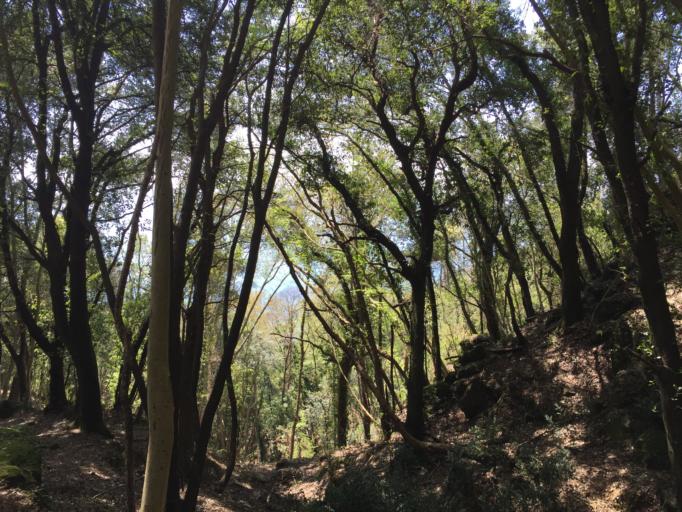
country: IT
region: Liguria
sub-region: Provincia di Genova
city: Santa Margherita Ligure
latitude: 44.3222
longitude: 9.1783
